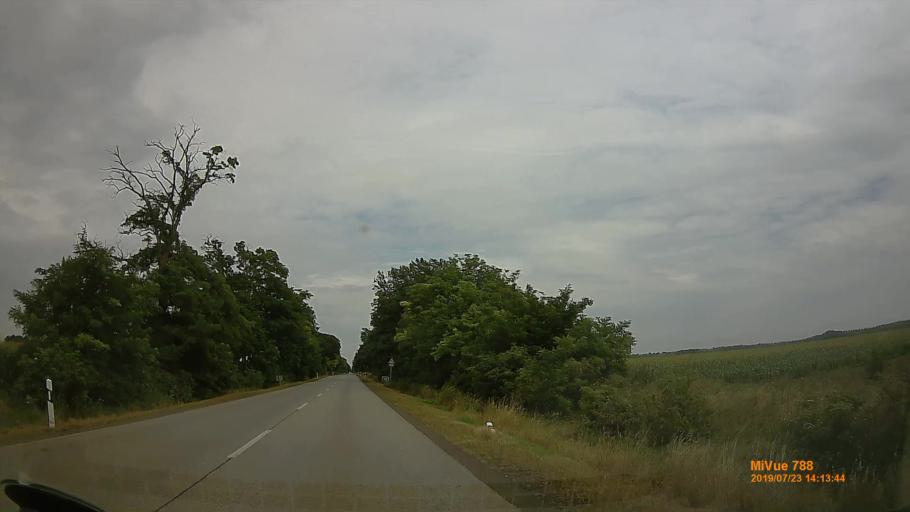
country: HU
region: Szabolcs-Szatmar-Bereg
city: Nagycserkesz
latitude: 47.9580
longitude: 21.4789
